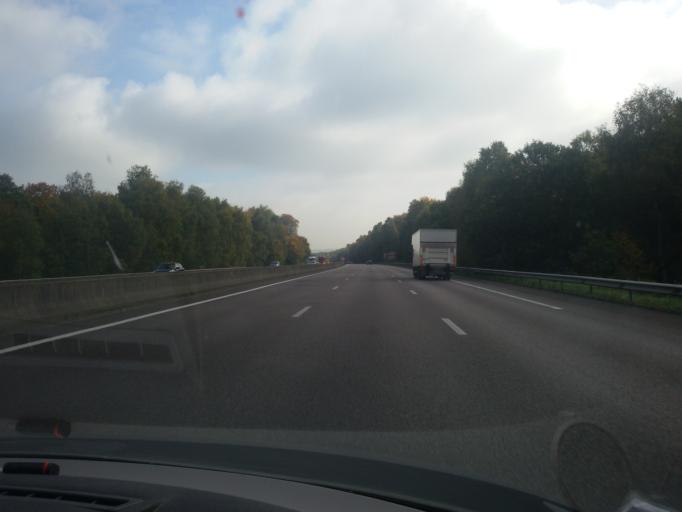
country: FR
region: Haute-Normandie
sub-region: Departement de l'Eure
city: Louviers
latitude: 49.2621
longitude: 1.1447
